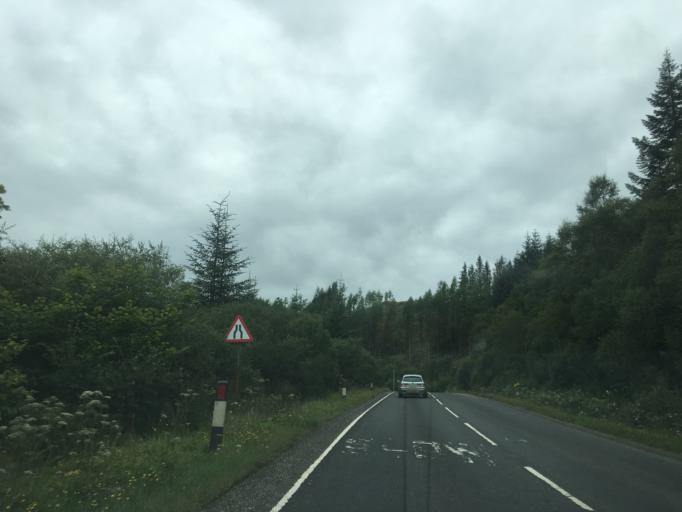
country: GB
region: Scotland
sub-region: Argyll and Bute
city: Oban
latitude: 56.3069
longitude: -5.4674
